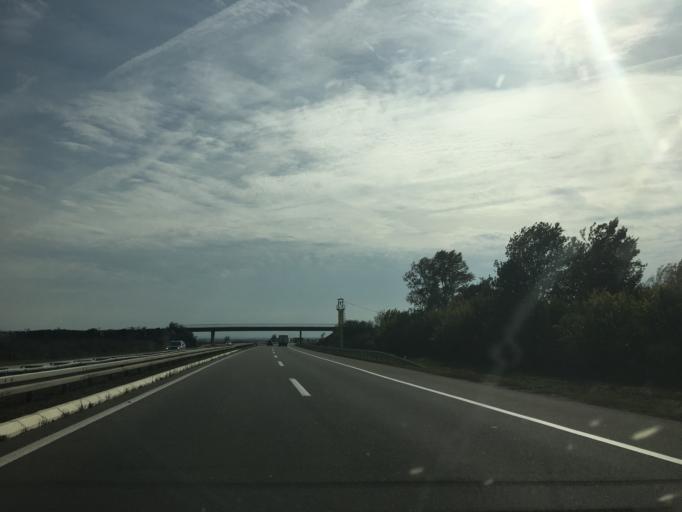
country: RS
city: Novi Banovci
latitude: 44.9181
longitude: 20.3048
